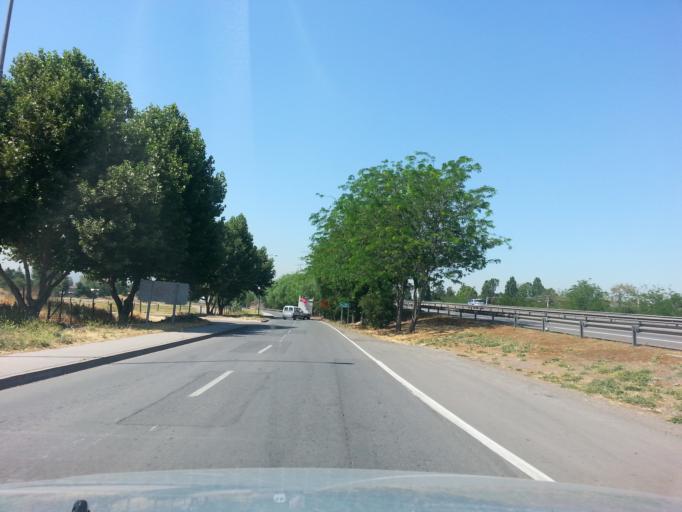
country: CL
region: Santiago Metropolitan
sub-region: Provincia de Chacabuco
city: Chicureo Abajo
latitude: -33.2389
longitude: -70.6968
